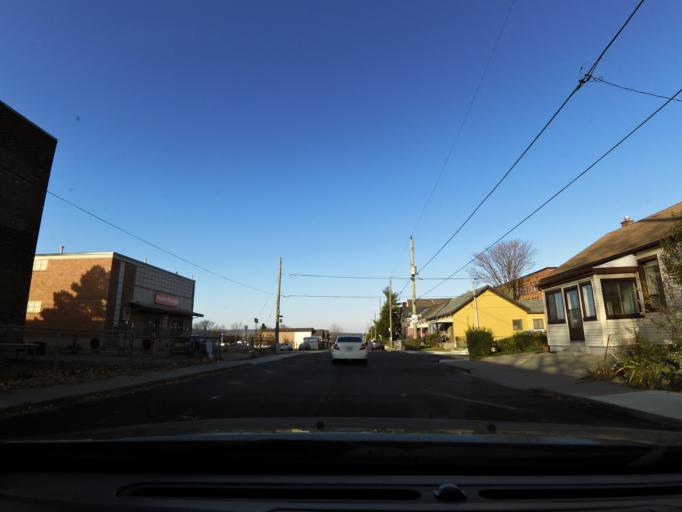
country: CA
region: Ontario
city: Hamilton
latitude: 43.2633
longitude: -79.8754
